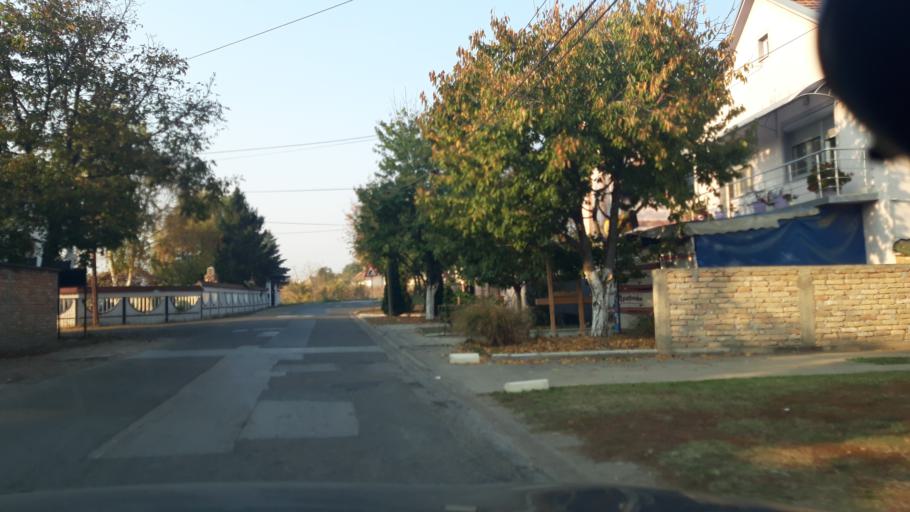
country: RS
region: Autonomna Pokrajina Vojvodina
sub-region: Sremski Okrug
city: Stara Pazova
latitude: 44.9967
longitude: 20.1445
